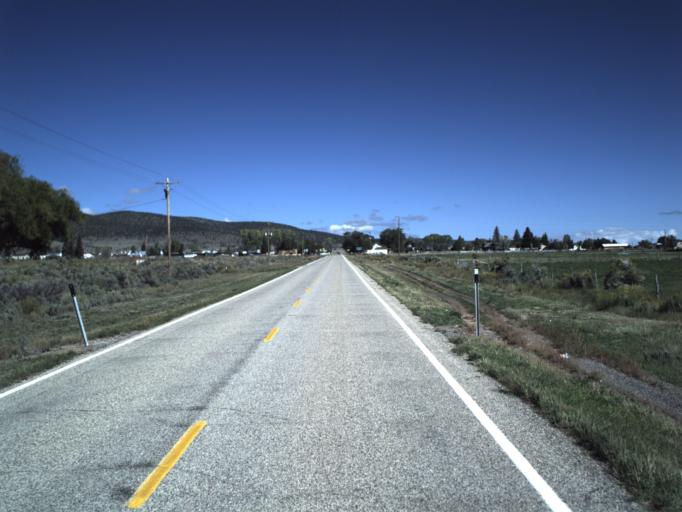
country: US
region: Utah
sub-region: Wayne County
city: Loa
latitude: 38.5002
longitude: -111.8813
